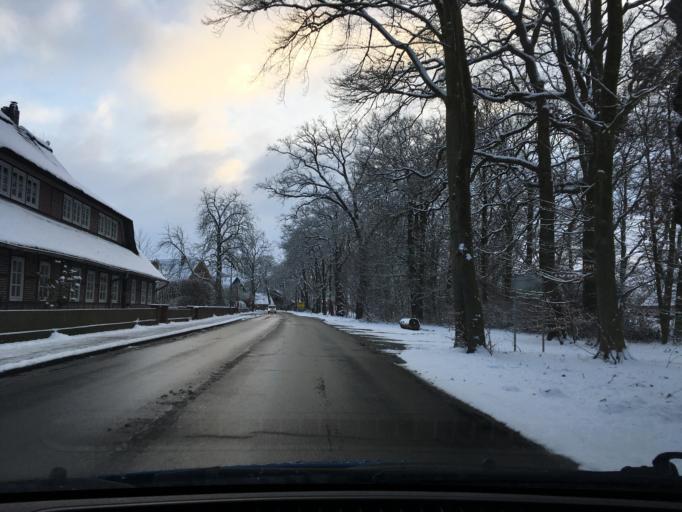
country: DE
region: Lower Saxony
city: Winsen
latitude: 53.3335
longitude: 10.1998
